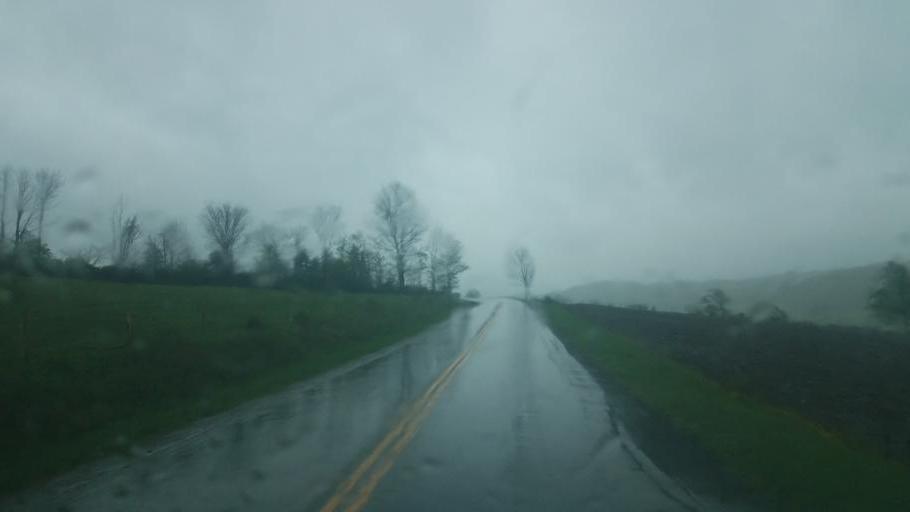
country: US
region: Pennsylvania
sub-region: Tioga County
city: Elkland
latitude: 42.0803
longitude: -77.4313
